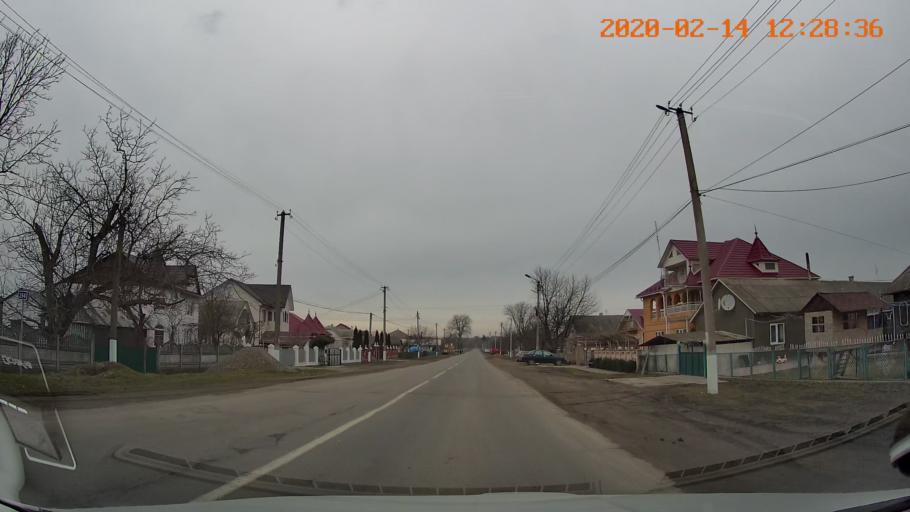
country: RO
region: Botosani
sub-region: Comuna Paltinis
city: Paltinis
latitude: 48.2579
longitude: 26.5949
